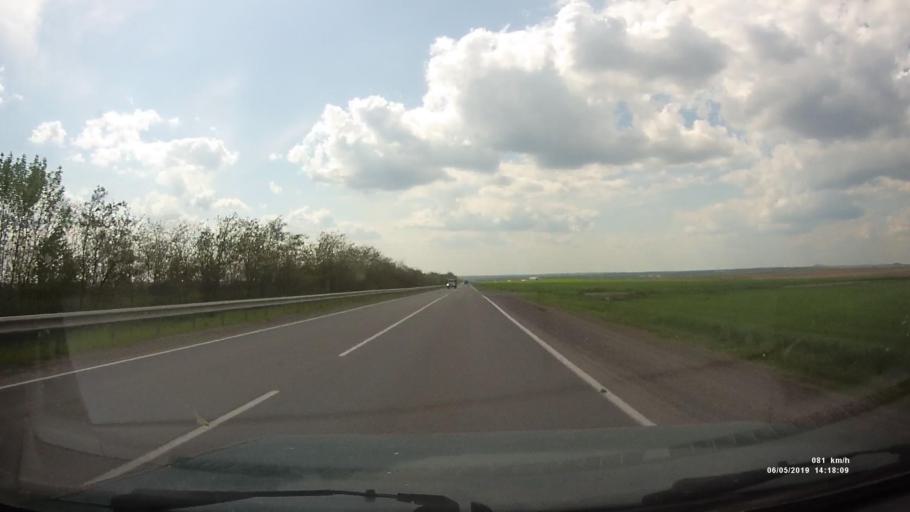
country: RU
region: Rostov
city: Kamenolomni
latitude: 47.6336
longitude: 40.2549
